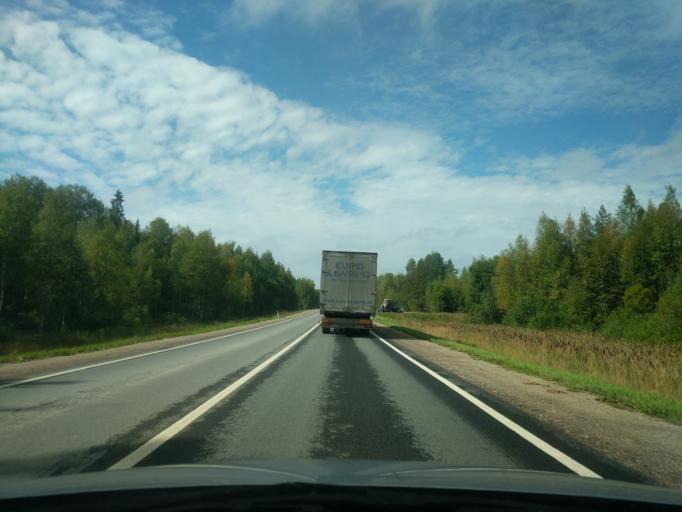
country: RU
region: Kostroma
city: Sudislavl'
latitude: 57.8464
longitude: 41.8186
